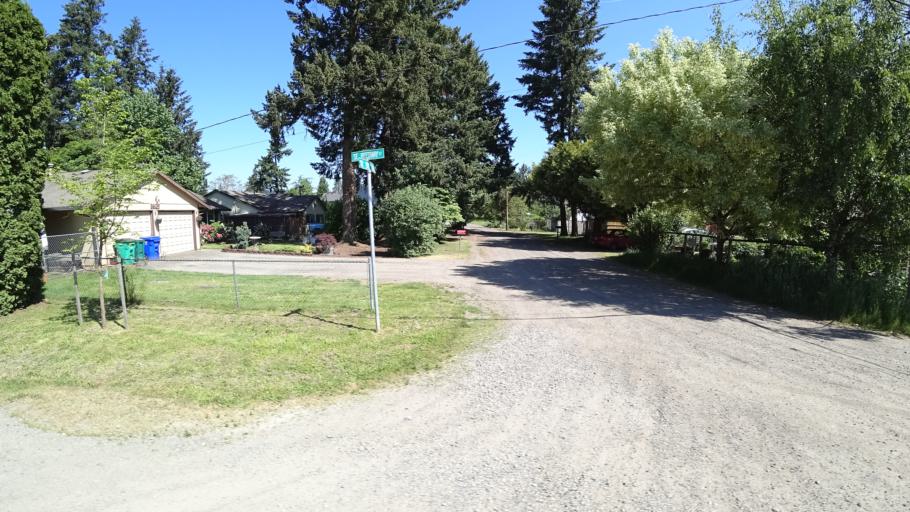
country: US
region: Oregon
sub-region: Multnomah County
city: Lents
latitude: 45.4813
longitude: -122.5431
